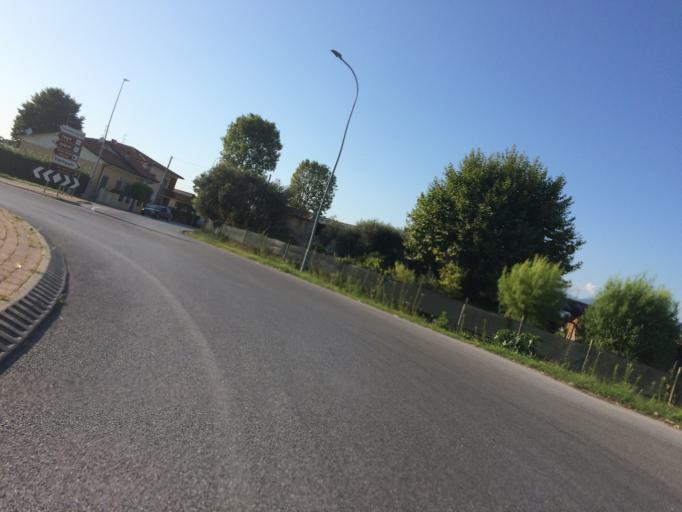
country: IT
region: Tuscany
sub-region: Provincia di Lucca
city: Torre del Lago Puccini
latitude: 43.8351
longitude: 10.2874
